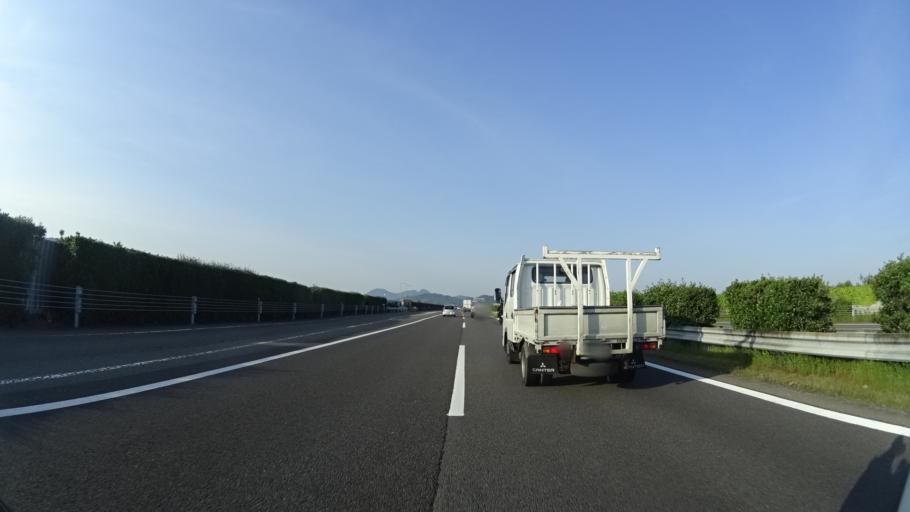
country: JP
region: Kagawa
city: Kan'onjicho
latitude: 34.1159
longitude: 133.6874
